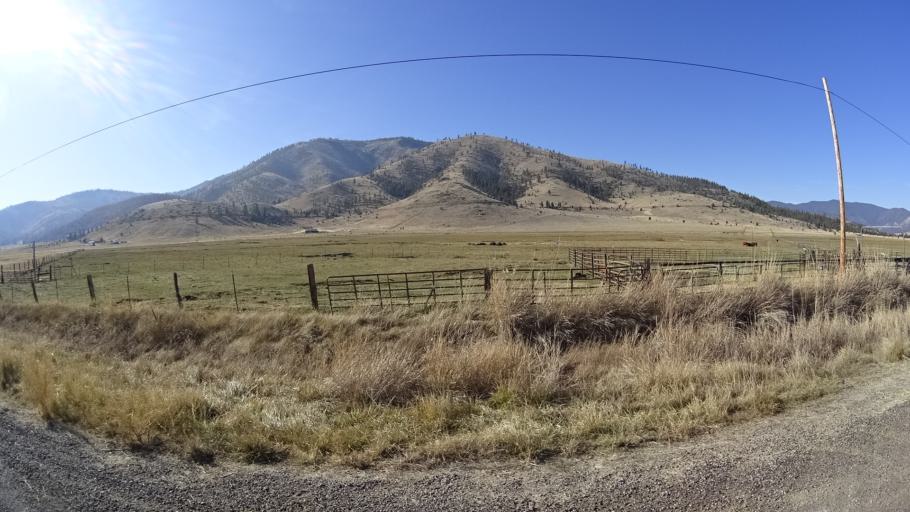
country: US
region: California
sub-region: Siskiyou County
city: Weed
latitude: 41.4867
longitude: -122.5017
